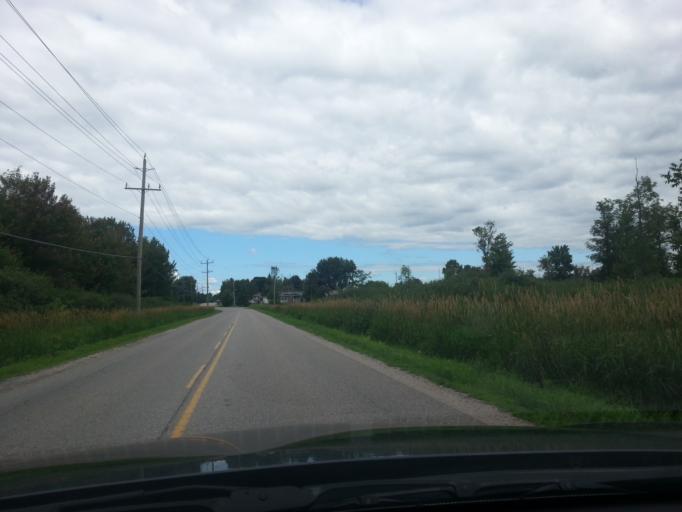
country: CA
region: Ontario
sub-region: Lanark County
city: Smiths Falls
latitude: 44.8850
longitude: -76.0533
